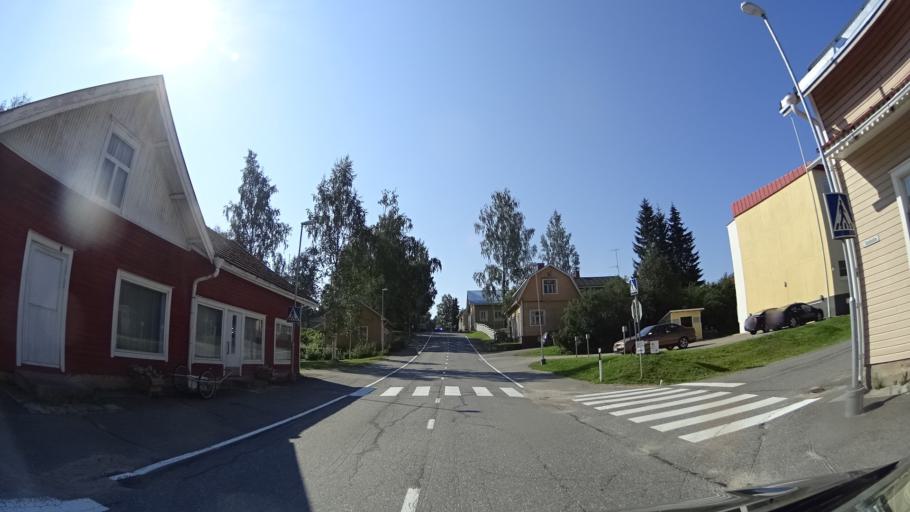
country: FI
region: North Karelia
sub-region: Joensuu
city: Juuka
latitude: 63.2424
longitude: 29.2499
